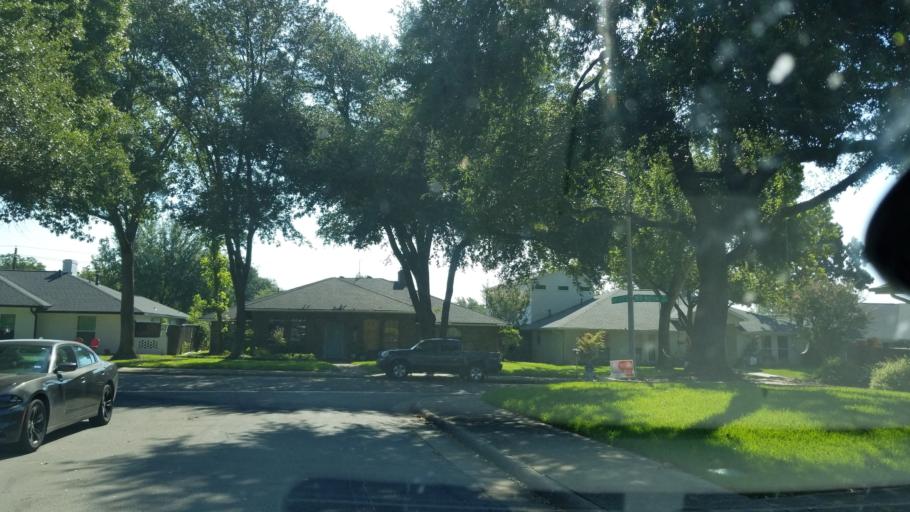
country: US
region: Texas
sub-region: Dallas County
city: Richardson
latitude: 32.9053
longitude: -96.7388
